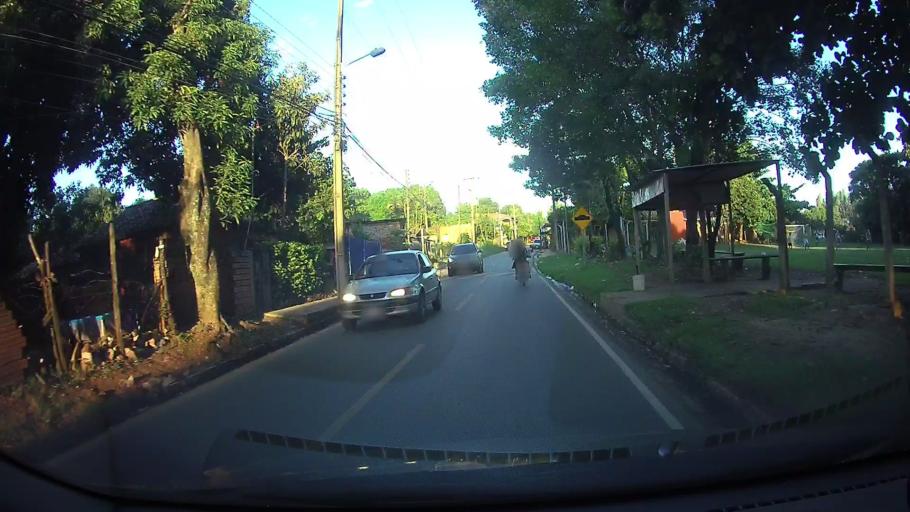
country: PY
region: Central
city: Fernando de la Mora
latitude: -25.2845
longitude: -57.5167
